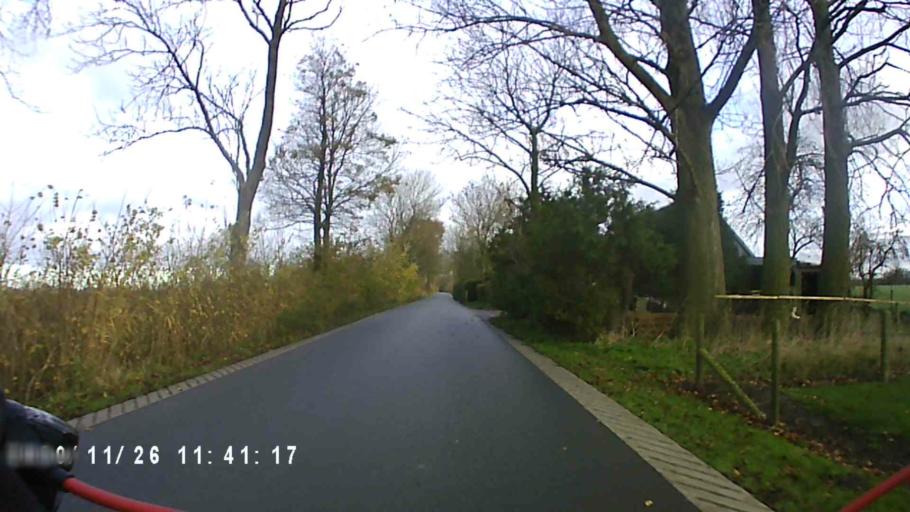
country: NL
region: Groningen
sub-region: Gemeente Bedum
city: Bedum
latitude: 53.2903
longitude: 6.5718
